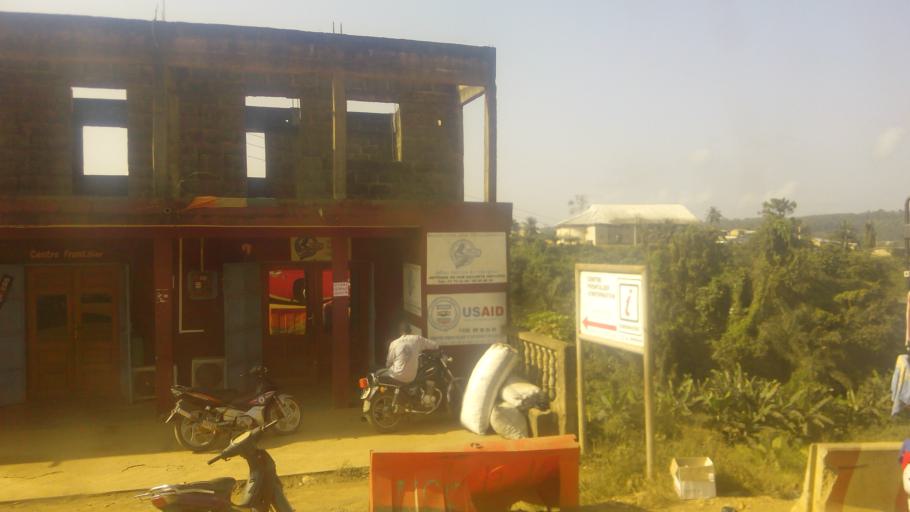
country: CI
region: Sud-Comoe
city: Mafere
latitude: 5.2905
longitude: -2.7906
